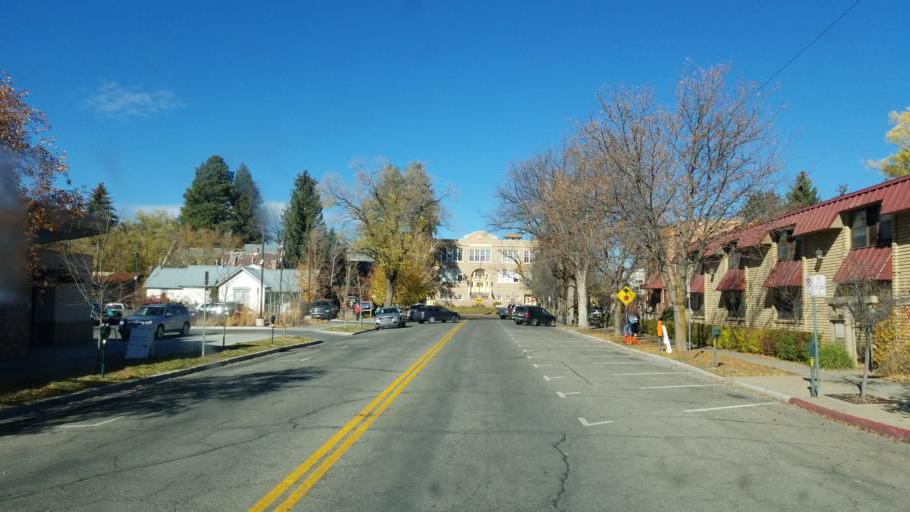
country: US
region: Colorado
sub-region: La Plata County
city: Durango
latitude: 37.2753
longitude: -107.8786
